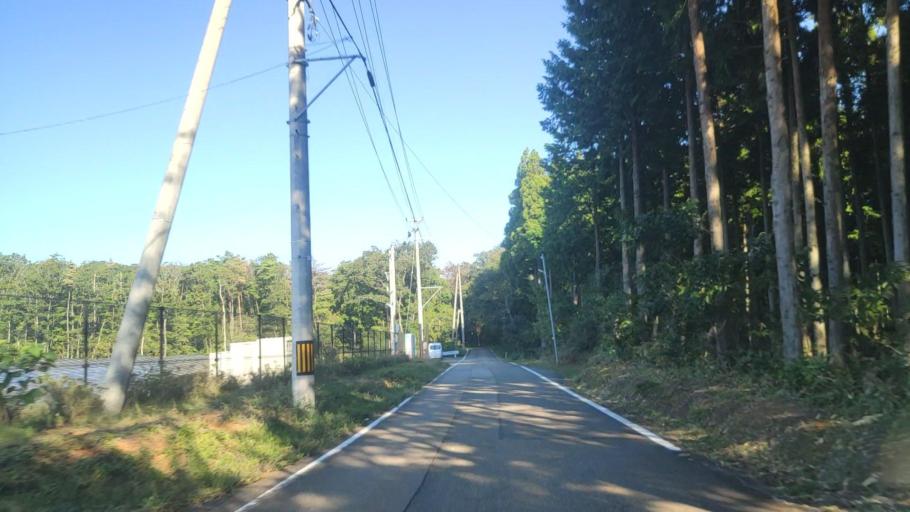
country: JP
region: Ishikawa
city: Nanao
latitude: 37.1173
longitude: 136.8888
